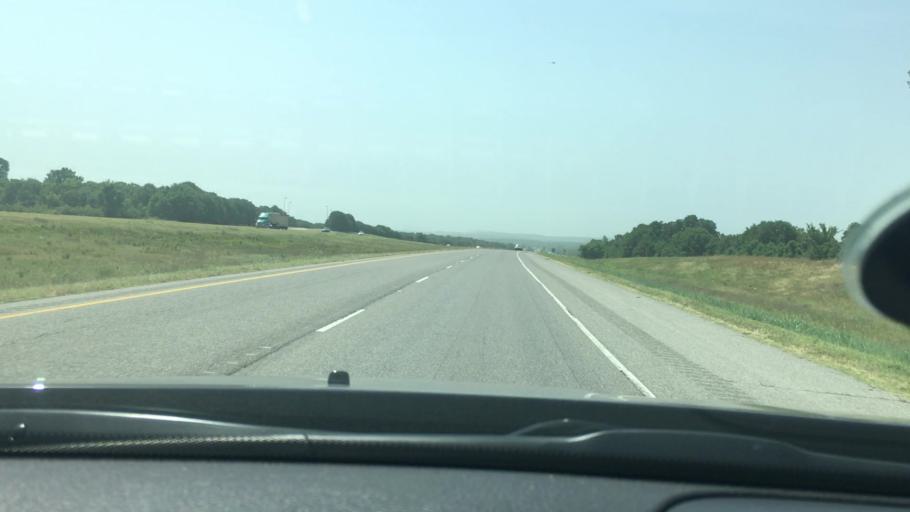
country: US
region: Oklahoma
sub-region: Murray County
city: Davis
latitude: 34.5560
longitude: -97.1925
